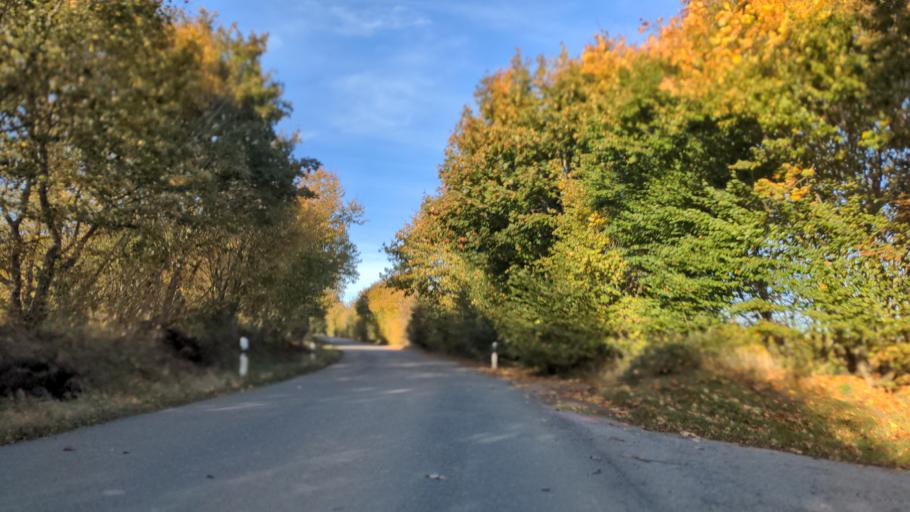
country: DE
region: Schleswig-Holstein
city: Kirchnuchel
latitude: 54.1665
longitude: 10.6696
